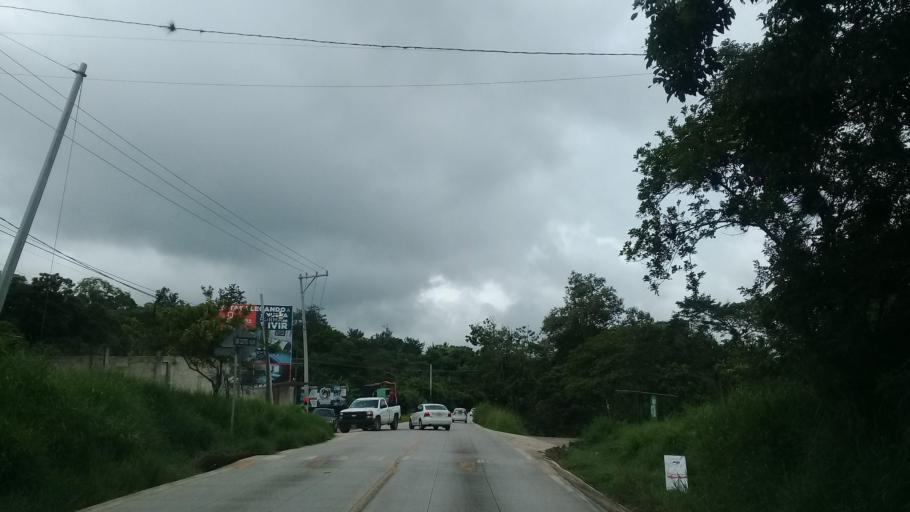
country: MX
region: Veracruz
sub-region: Emiliano Zapata
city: Jacarandas
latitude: 19.4822
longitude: -96.8572
